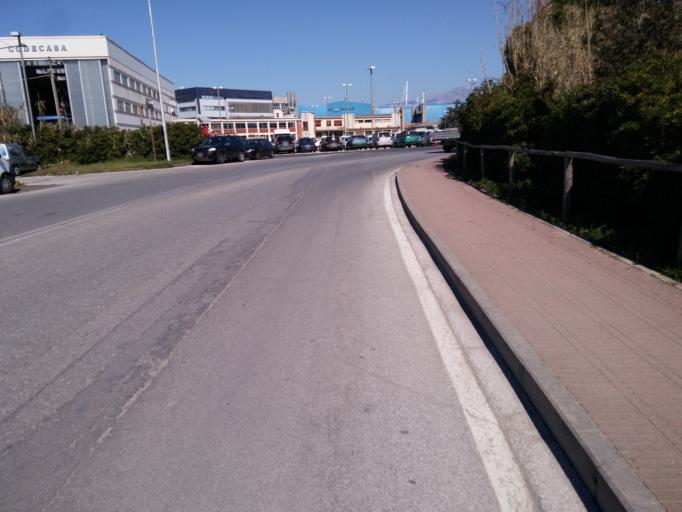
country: IT
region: Tuscany
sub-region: Provincia di Lucca
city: Viareggio
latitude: 43.8573
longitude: 10.2444
